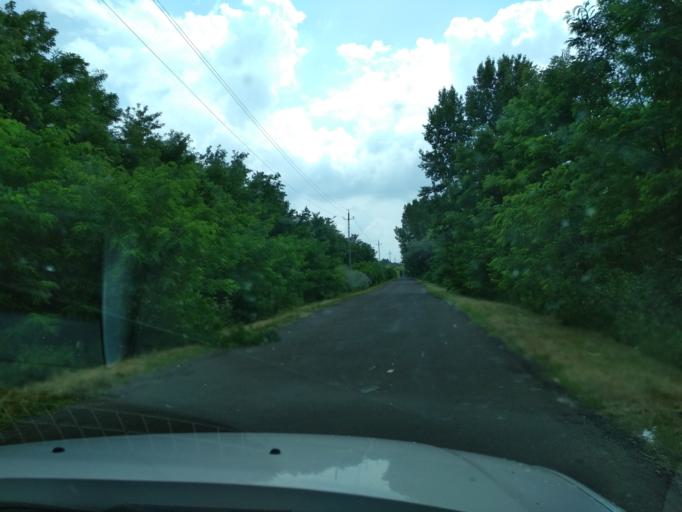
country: HU
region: Pest
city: Nagykata
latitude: 47.3867
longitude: 19.7561
